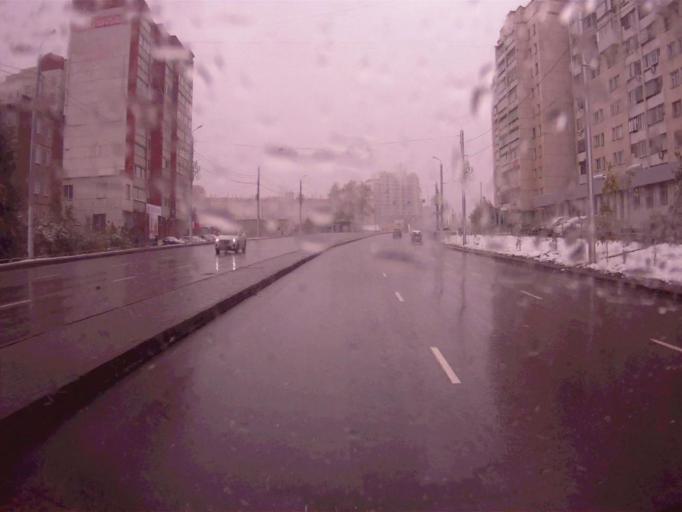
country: RU
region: Chelyabinsk
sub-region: Gorod Chelyabinsk
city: Chelyabinsk
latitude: 55.1431
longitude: 61.4079
